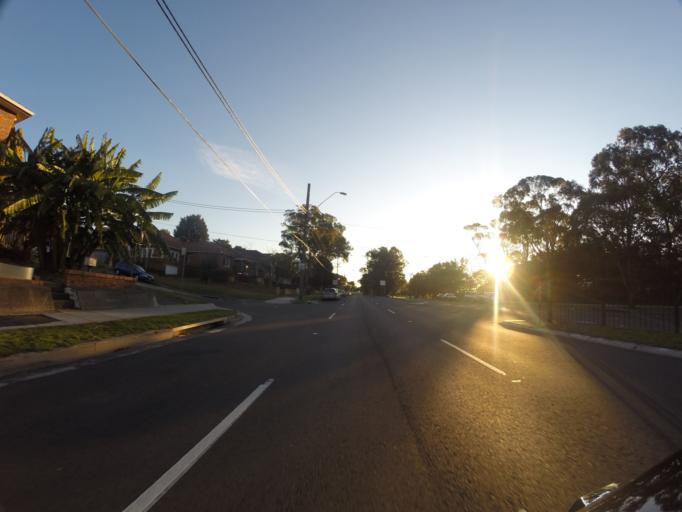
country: AU
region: New South Wales
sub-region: Sutherland Shire
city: Miranda
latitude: -34.0337
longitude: 151.0963
